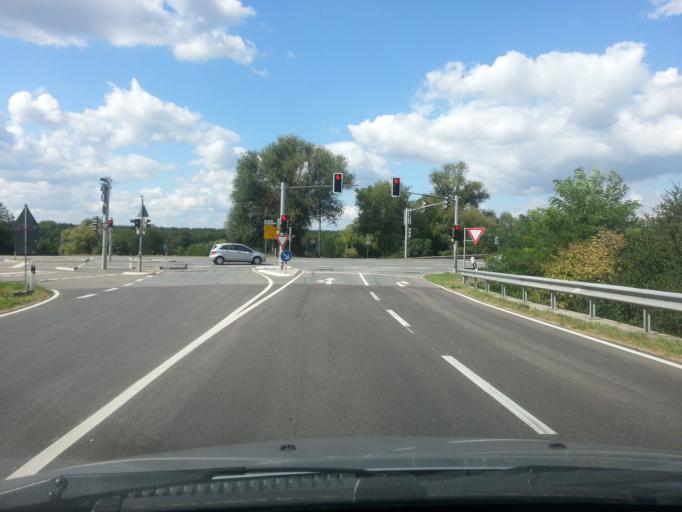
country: DE
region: Baden-Wuerttemberg
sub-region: Karlsruhe Region
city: Malsch
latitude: 49.2604
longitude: 8.6680
